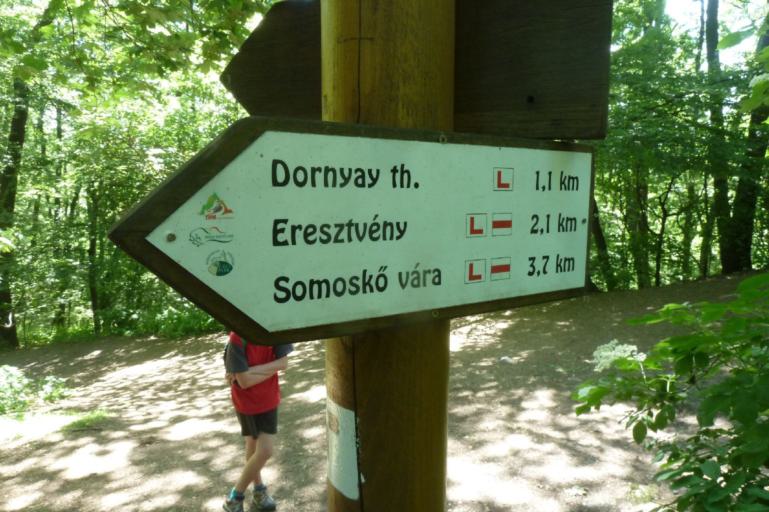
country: HU
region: Nograd
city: Somoskoujfalu
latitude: 48.1440
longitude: 19.8482
